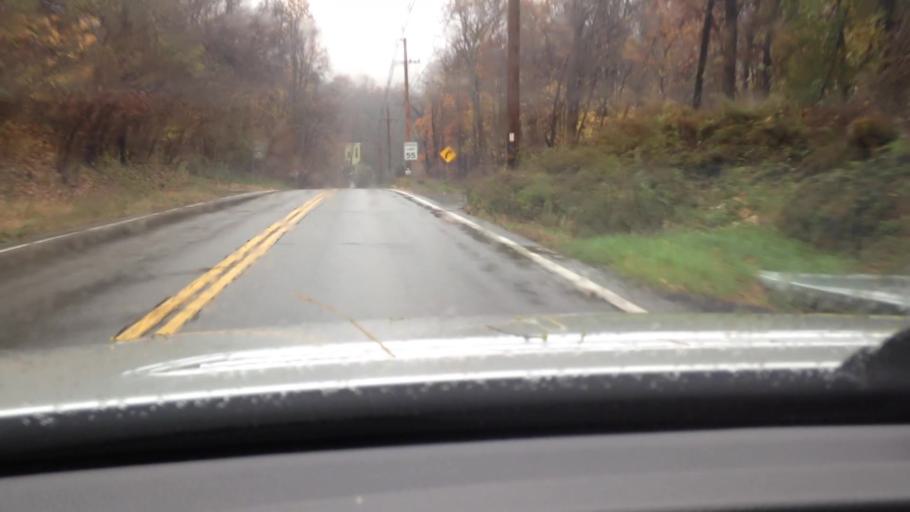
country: US
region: New York
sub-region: Dutchess County
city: Beacon
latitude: 41.4702
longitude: -73.9757
